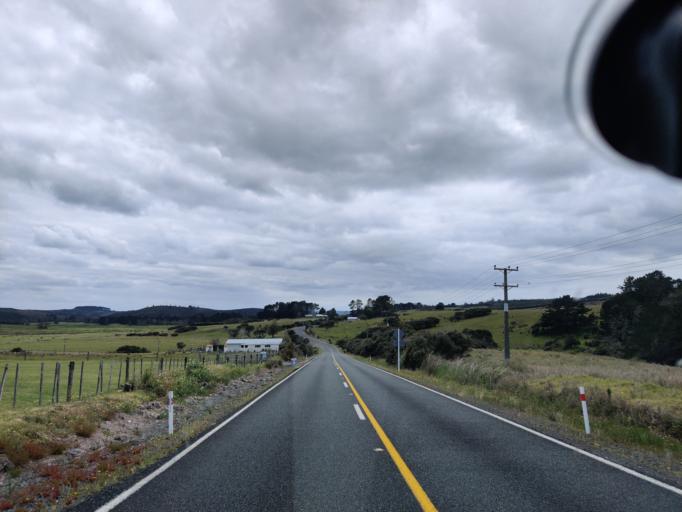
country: NZ
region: Northland
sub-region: Far North District
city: Kaitaia
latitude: -34.6443
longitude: 172.9701
